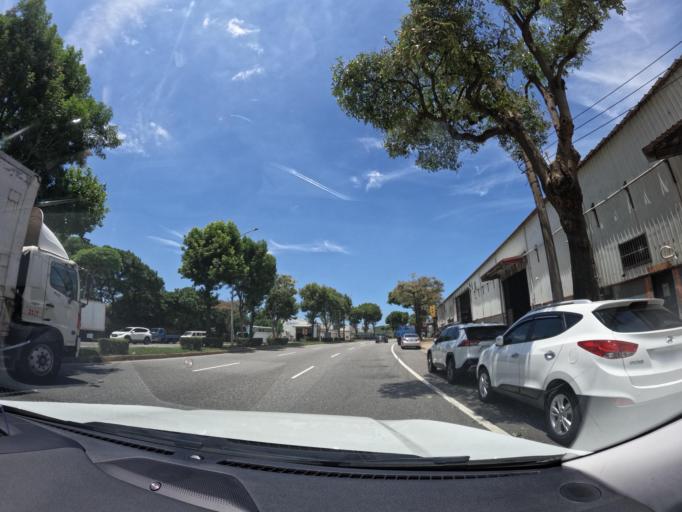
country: TW
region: Taiwan
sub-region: Taoyuan
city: Taoyuan
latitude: 25.0586
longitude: 121.3540
